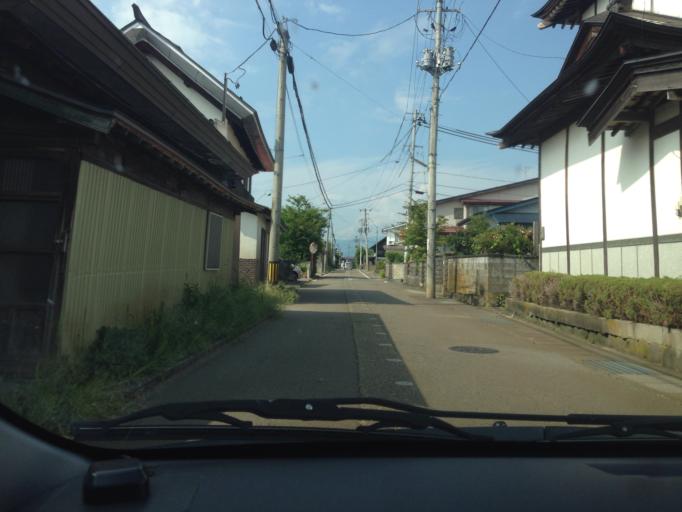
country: JP
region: Fukushima
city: Kitakata
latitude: 37.5872
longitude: 139.8864
